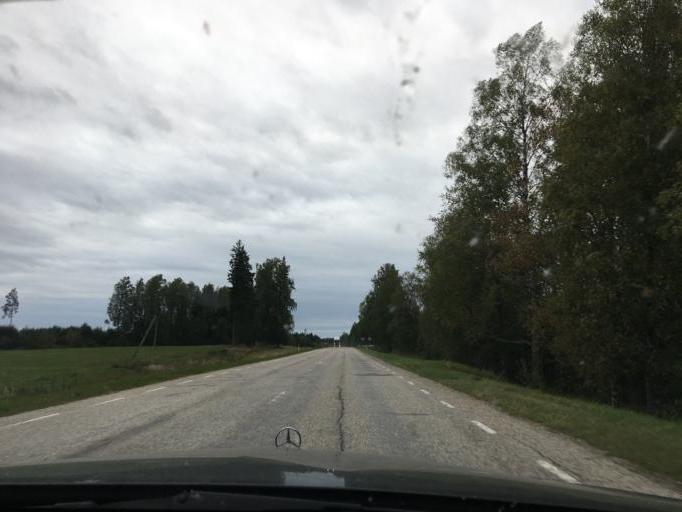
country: LV
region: Aluksnes Rajons
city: Aluksne
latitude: 57.5999
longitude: 27.1592
